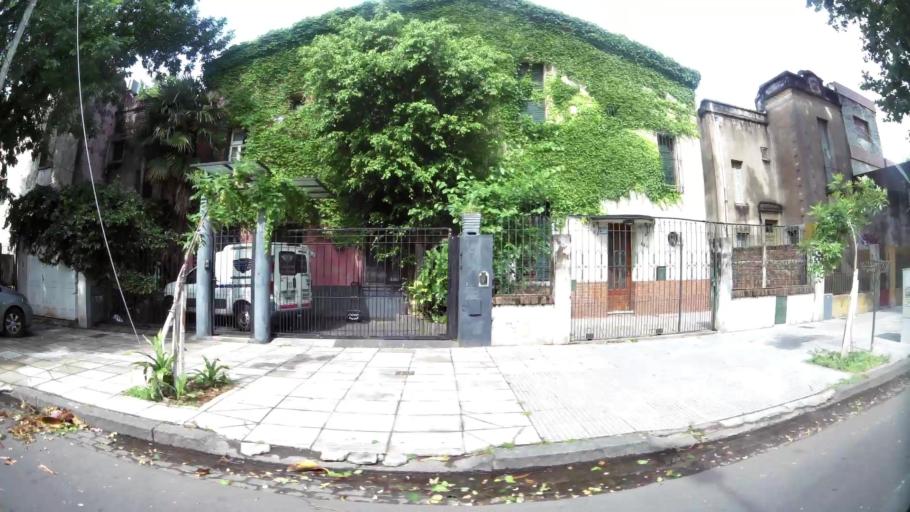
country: AR
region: Buenos Aires
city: San Justo
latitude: -34.6463
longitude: -58.5244
